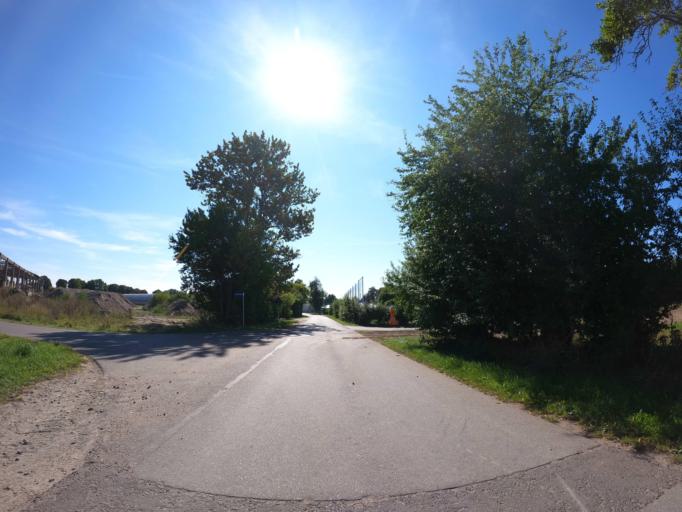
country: DE
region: Mecklenburg-Vorpommern
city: Prohn
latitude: 54.3791
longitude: 13.0225
